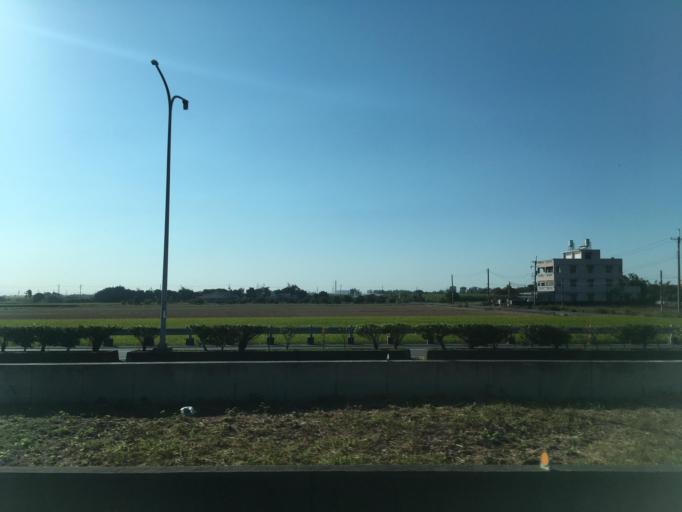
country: TW
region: Taiwan
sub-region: Chiayi
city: Taibao
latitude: 23.4475
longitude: 120.3233
